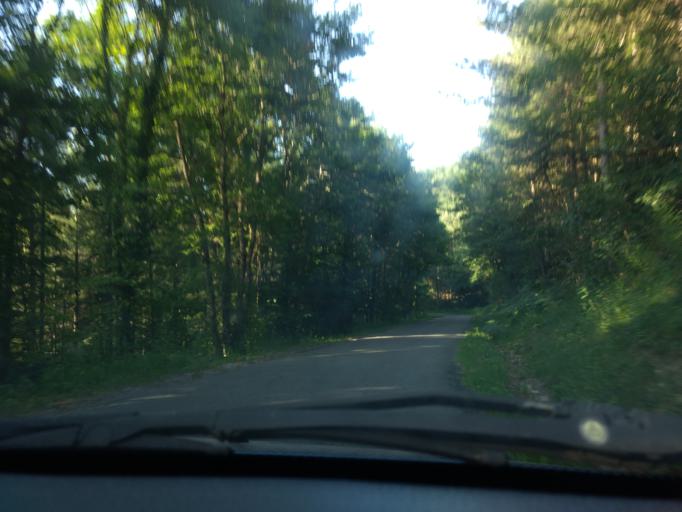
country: FR
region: Midi-Pyrenees
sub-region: Departement de l'Aveyron
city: La Loubiere
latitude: 44.3794
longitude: 2.7105
